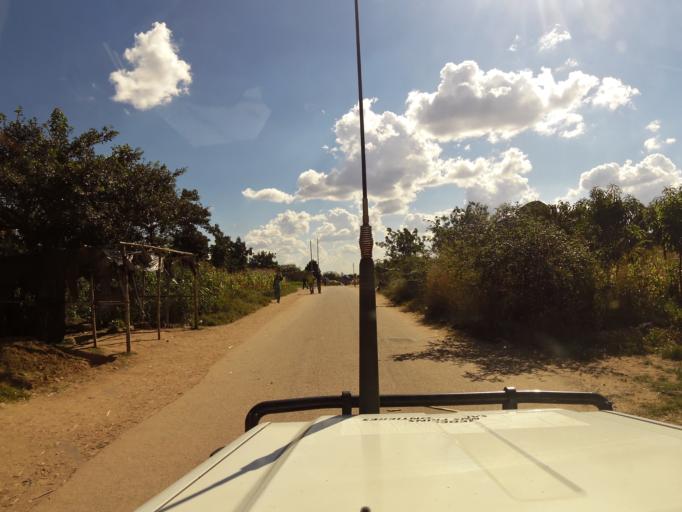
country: ZW
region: Harare
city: Epworth
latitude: -17.8751
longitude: 31.1387
